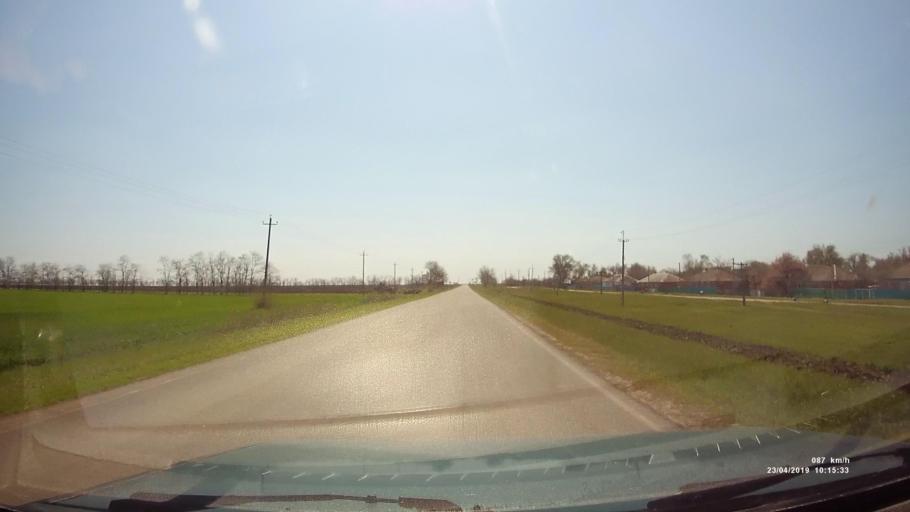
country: RU
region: Rostov
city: Sovetskoye
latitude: 46.6659
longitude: 42.3833
